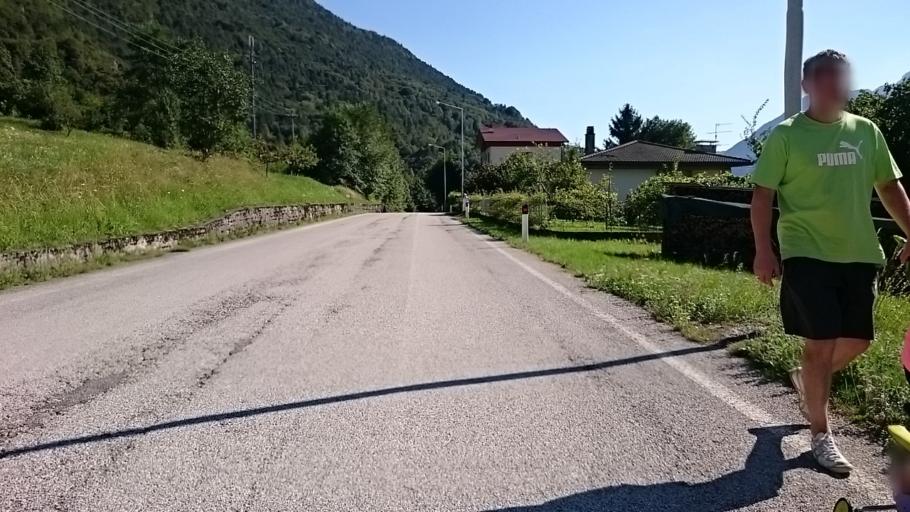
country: IT
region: Veneto
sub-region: Provincia di Belluno
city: Longarone
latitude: 46.2426
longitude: 12.3120
